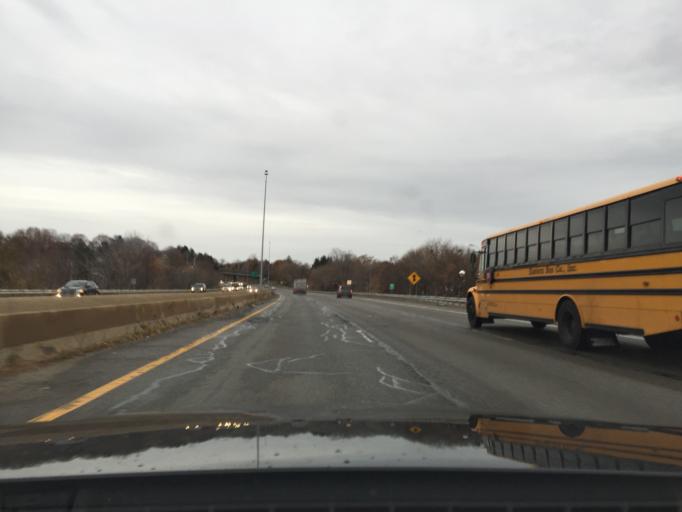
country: US
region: Massachusetts
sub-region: Suffolk County
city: Revere
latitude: 42.4210
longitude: -71.0286
